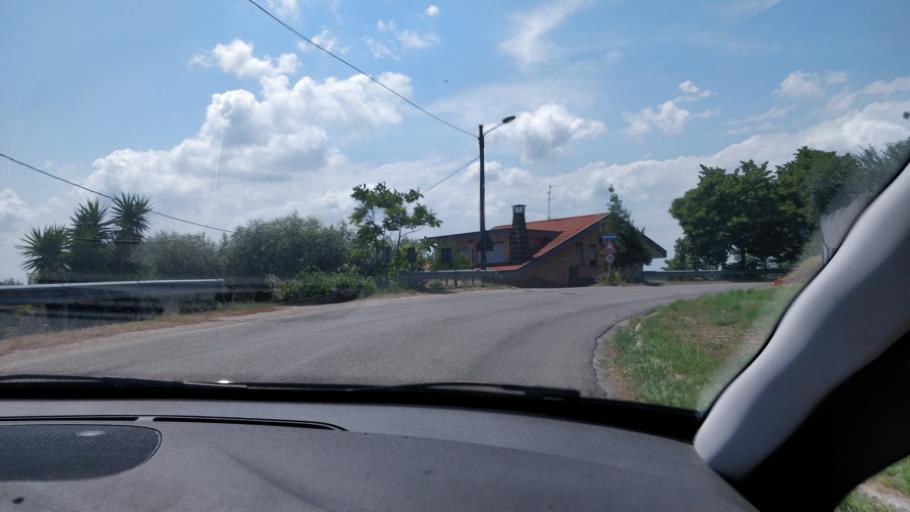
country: IT
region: Abruzzo
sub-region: Provincia di Chieti
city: Francavilla al Mare
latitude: 42.4208
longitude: 14.2489
